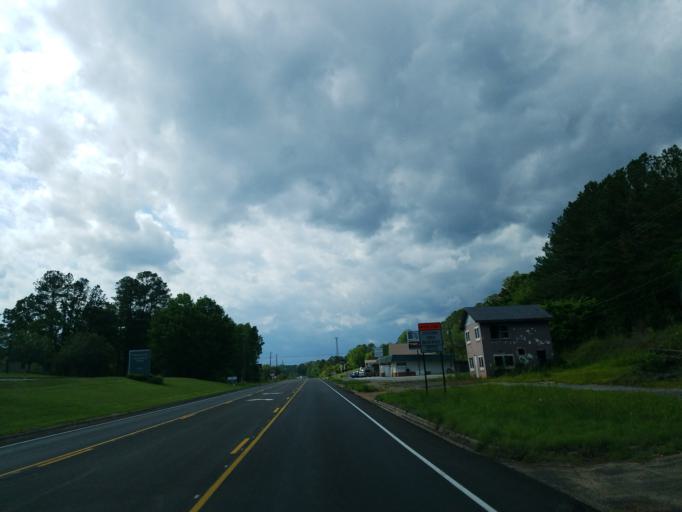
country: US
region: Georgia
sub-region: Pickens County
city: Jasper
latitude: 34.4587
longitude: -84.4120
